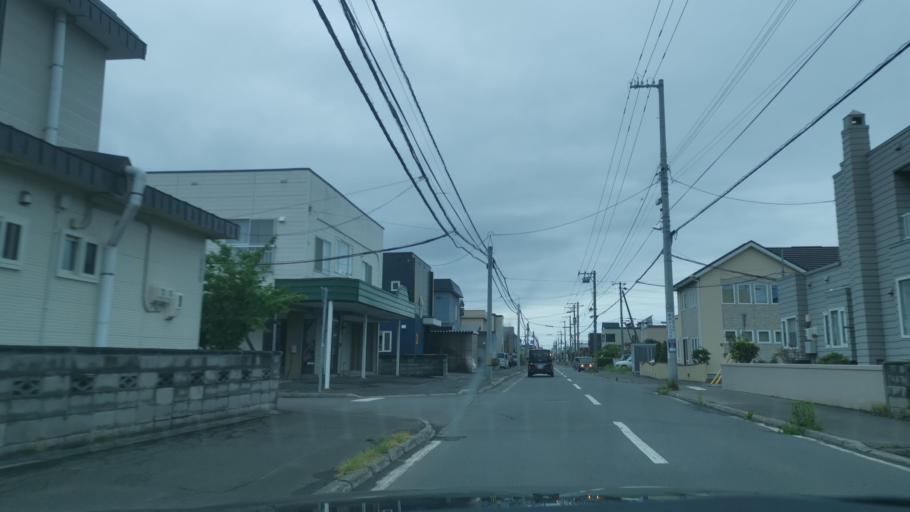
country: JP
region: Hokkaido
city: Sapporo
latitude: 43.1034
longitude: 141.3101
